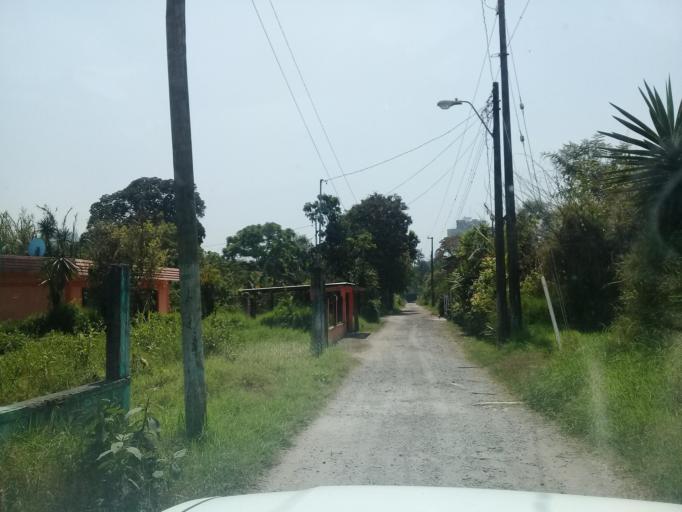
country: MX
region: Veracruz
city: Ixtac Zoquitlan
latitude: 18.8635
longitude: -97.0412
